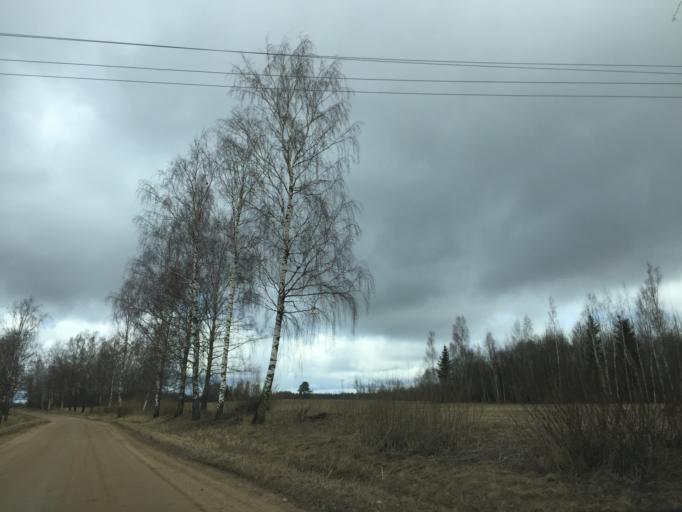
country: LV
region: Ilukste
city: Ilukste
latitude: 56.0755
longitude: 26.0457
